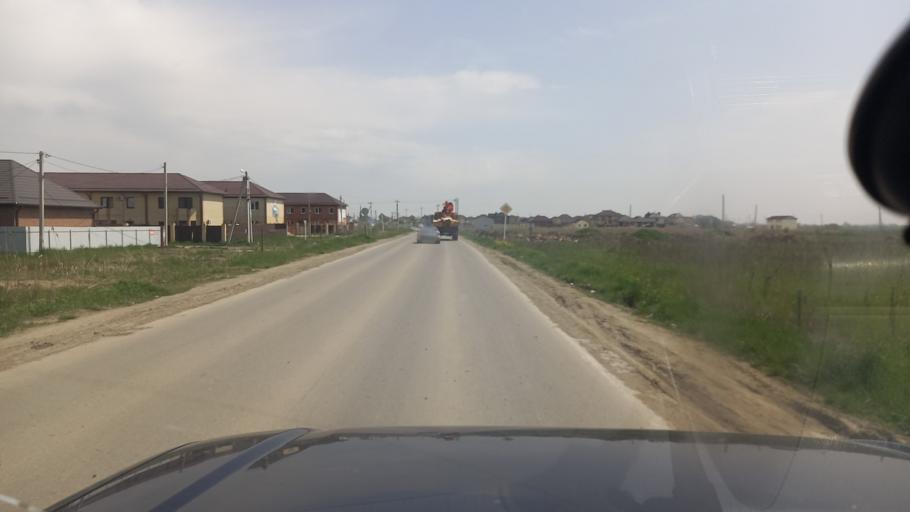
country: RU
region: Adygeya
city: Yablonovskiy
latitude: 44.9854
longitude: 38.9686
